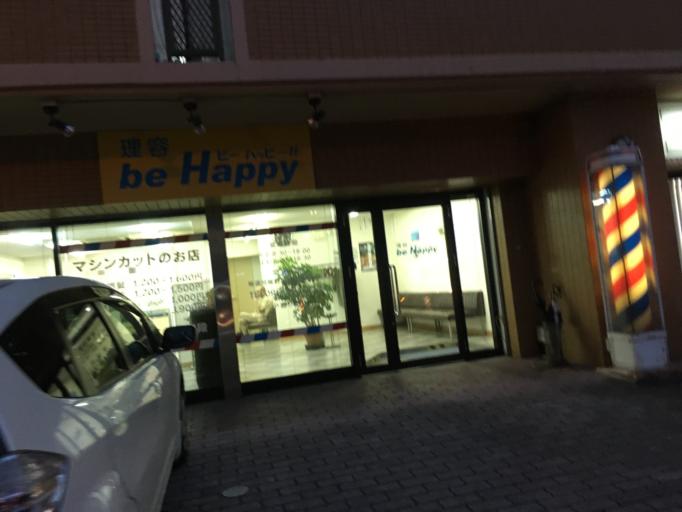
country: JP
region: Kumamoto
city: Kumamoto
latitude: 32.7939
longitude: 130.7272
